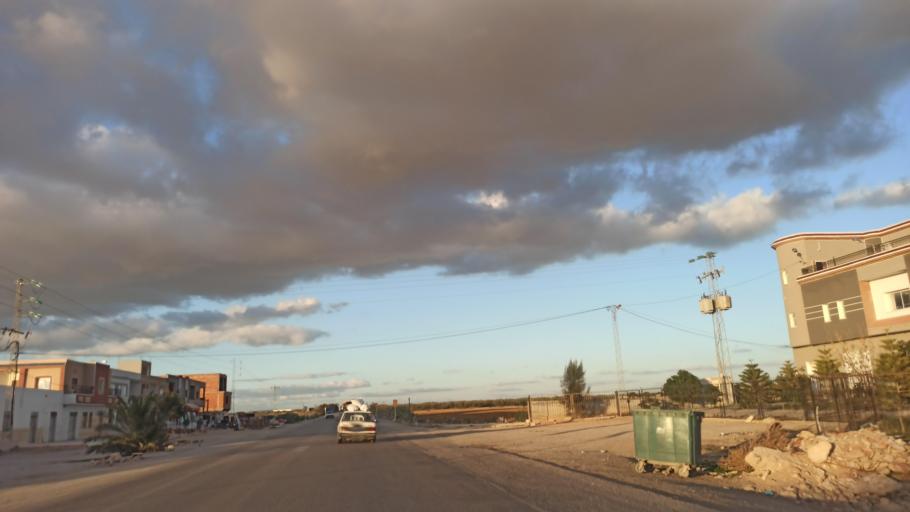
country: TN
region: Susah
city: Sidi Bou Ali
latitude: 36.0114
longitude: 10.3181
